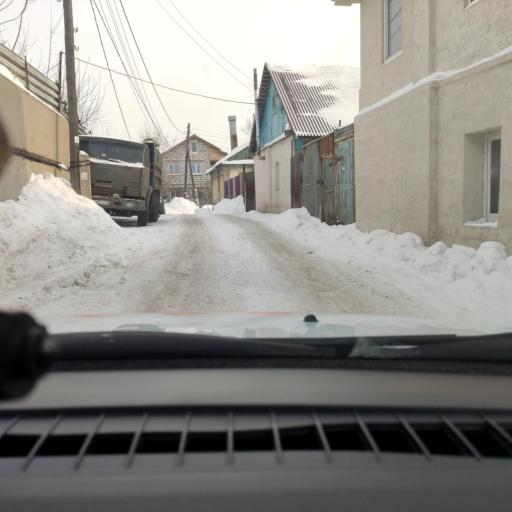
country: RU
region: Samara
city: Rozhdestveno
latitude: 53.1647
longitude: 50.0726
